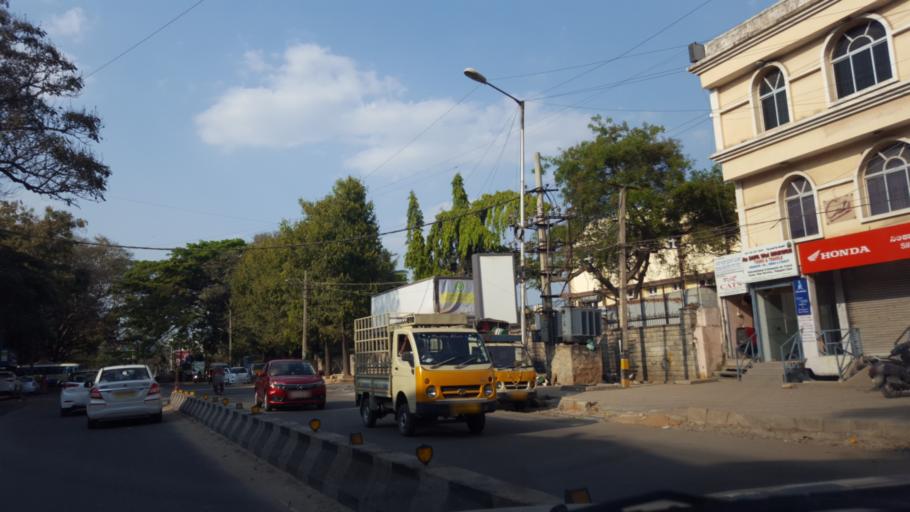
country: IN
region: Karnataka
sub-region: Bangalore Urban
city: Bangalore
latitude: 12.9260
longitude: 77.5971
